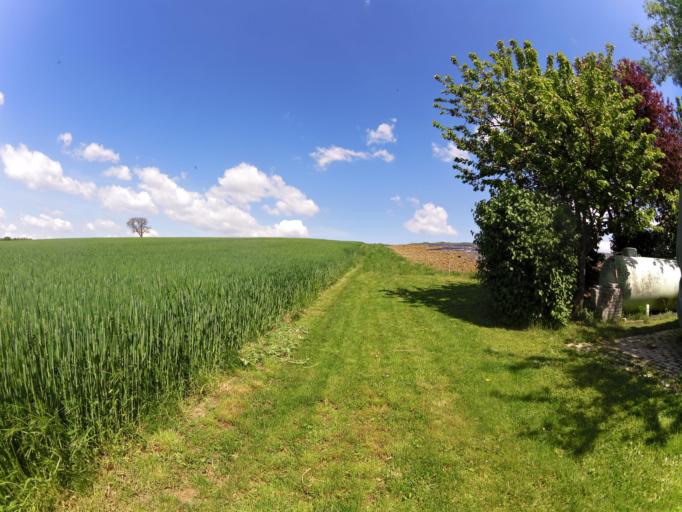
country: DE
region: Bavaria
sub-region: Regierungsbezirk Unterfranken
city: Unterpleichfeld
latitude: 49.8855
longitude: 10.0085
